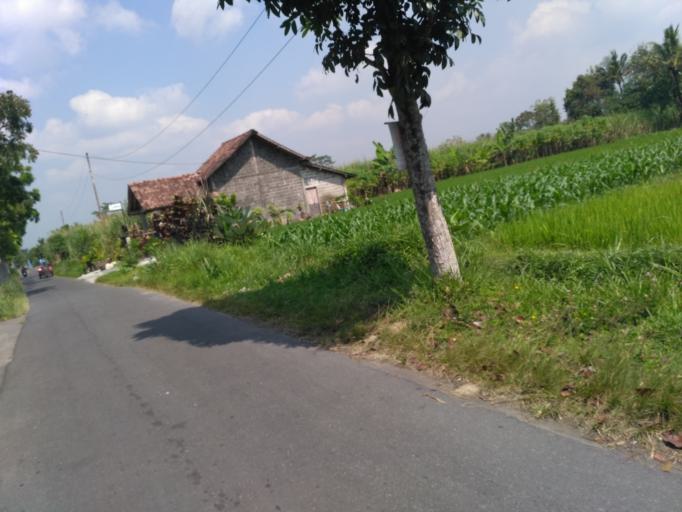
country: ID
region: Daerah Istimewa Yogyakarta
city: Depok
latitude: -7.7115
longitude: 110.4240
